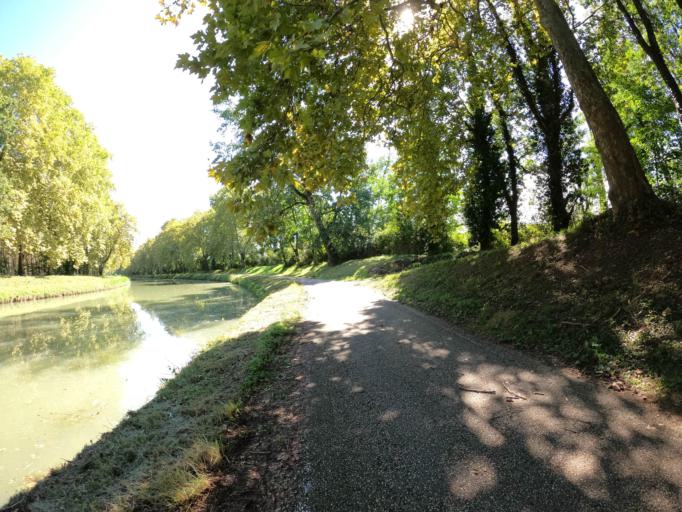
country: FR
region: Midi-Pyrenees
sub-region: Departement du Tarn-et-Garonne
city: Valence
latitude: 44.1121
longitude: 0.8718
